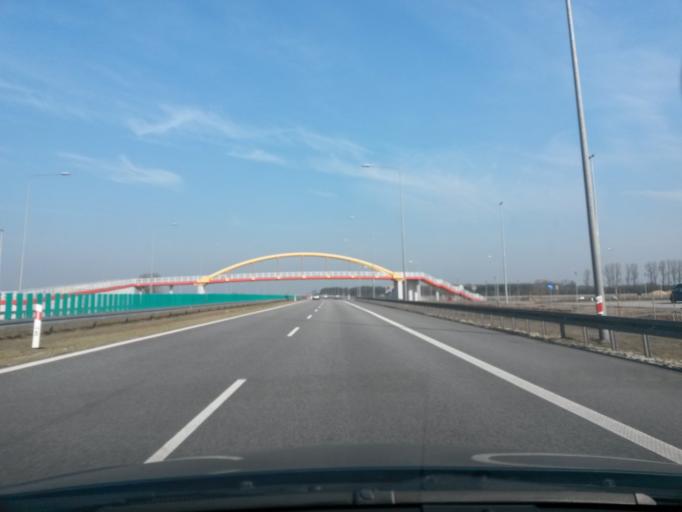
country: PL
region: Lodz Voivodeship
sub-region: Powiat kutnowski
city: Krzyzanow
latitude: 52.1846
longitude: 19.4876
